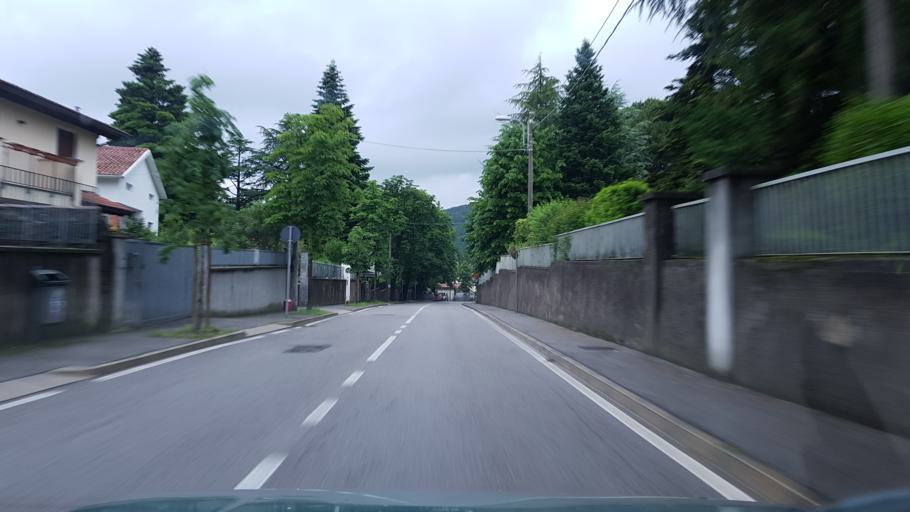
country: IT
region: Friuli Venezia Giulia
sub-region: Provincia di Gorizia
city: Gorizia
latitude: 45.9534
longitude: 13.6184
